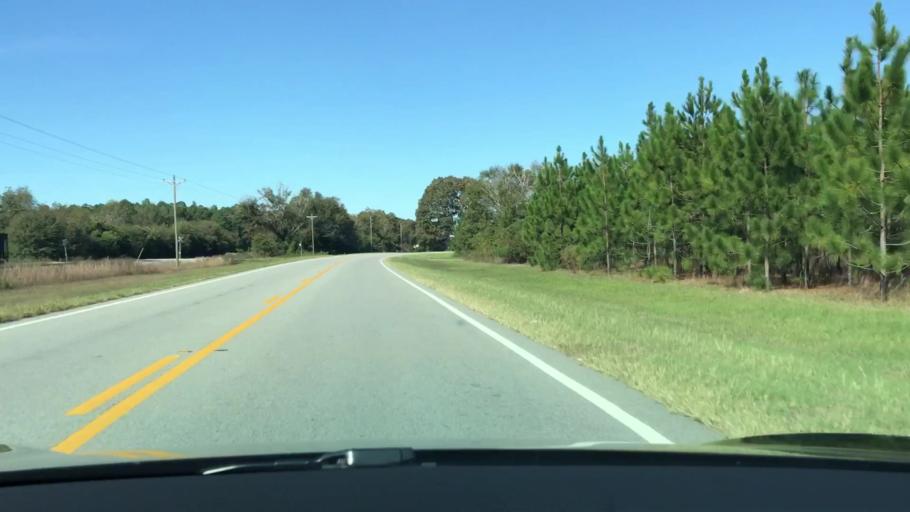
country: US
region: Georgia
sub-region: Glascock County
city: Gibson
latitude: 33.3073
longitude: -82.5307
